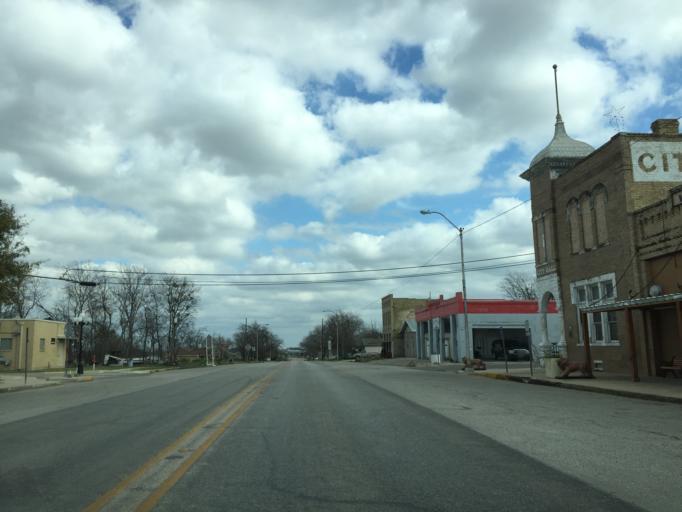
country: US
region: Texas
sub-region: Williamson County
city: Granger
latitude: 30.7175
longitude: -97.4411
